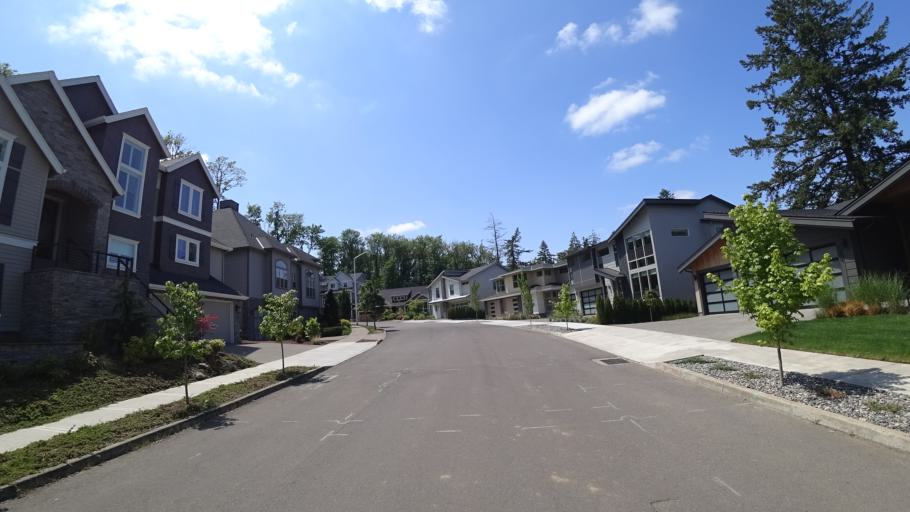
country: US
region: Oregon
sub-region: Clackamas County
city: Lake Oswego
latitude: 45.4369
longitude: -122.6920
